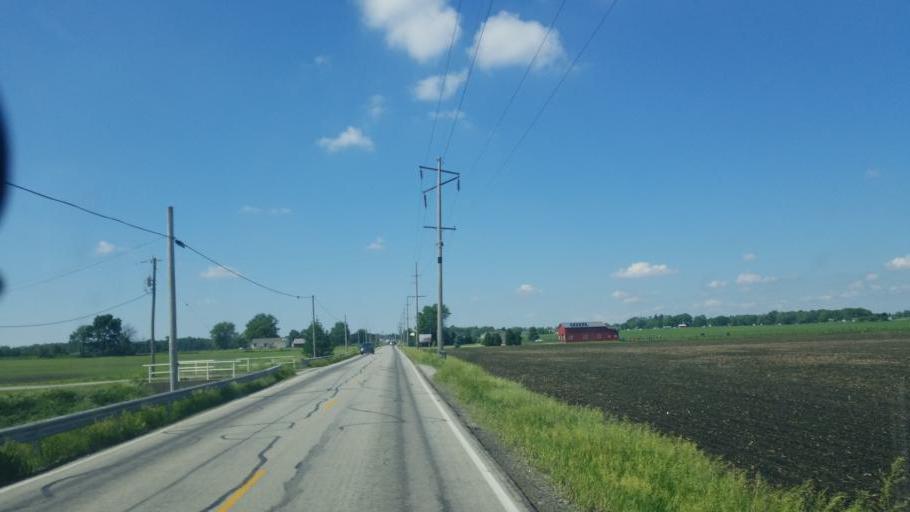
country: US
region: Indiana
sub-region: Elkhart County
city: Nappanee
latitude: 41.4165
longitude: -86.0012
